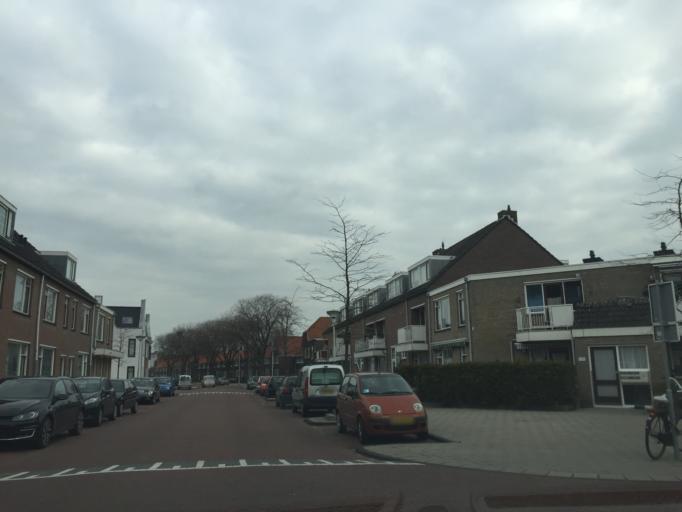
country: NL
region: South Holland
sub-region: Gemeente Leiden
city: Leiden
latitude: 52.1653
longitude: 4.4988
